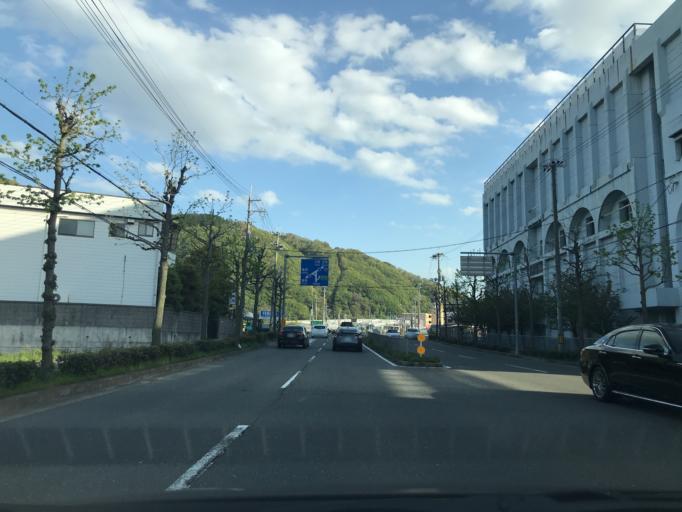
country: JP
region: Osaka
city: Ikeda
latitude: 34.8425
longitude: 135.4241
